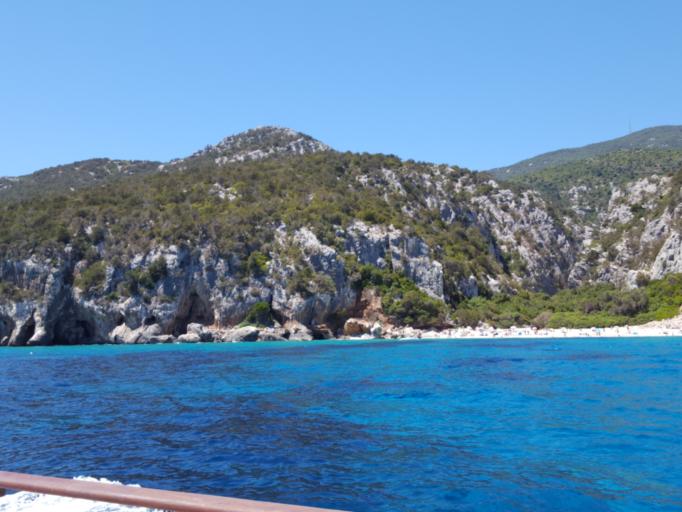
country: IT
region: Sardinia
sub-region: Provincia di Nuoro
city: Cala Gonone
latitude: 40.2558
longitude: 9.6278
